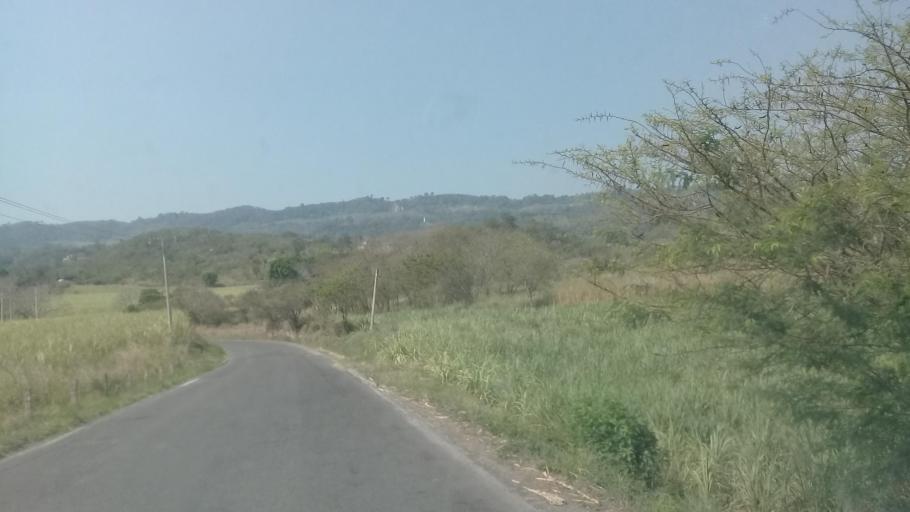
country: MX
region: Veracruz
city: El Castillo
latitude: 19.5816
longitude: -96.8289
